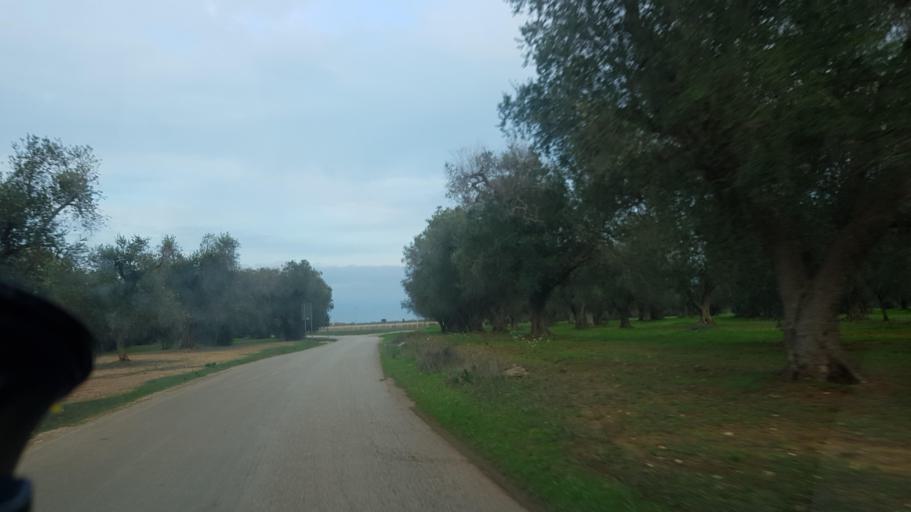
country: IT
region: Apulia
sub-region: Provincia di Brindisi
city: Mesagne
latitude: 40.5363
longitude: 17.7674
